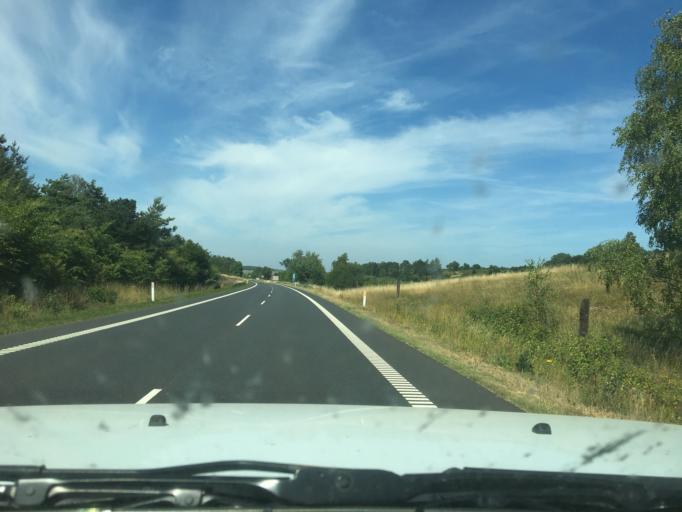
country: DK
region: Central Jutland
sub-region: Viborg Kommune
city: Viborg
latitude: 56.5190
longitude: 9.4039
